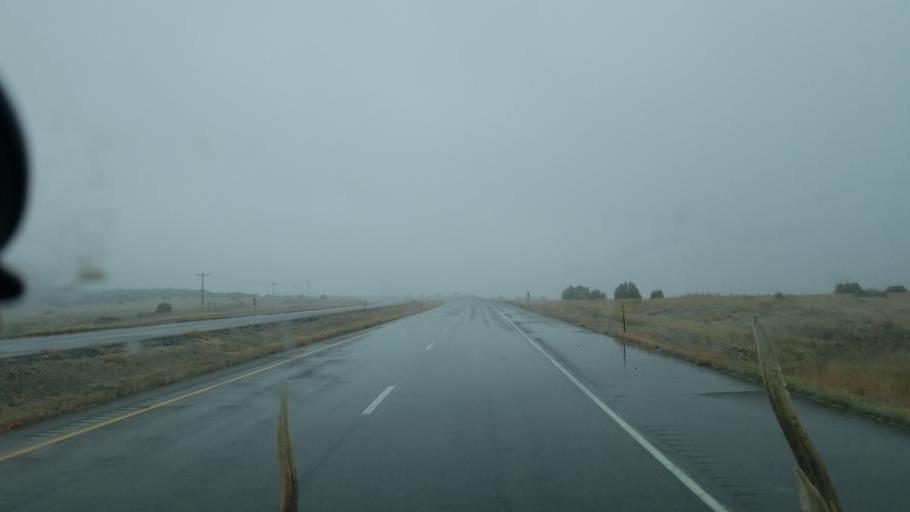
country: US
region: Colorado
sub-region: Pueblo County
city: Colorado City
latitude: 38.0263
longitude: -104.7337
